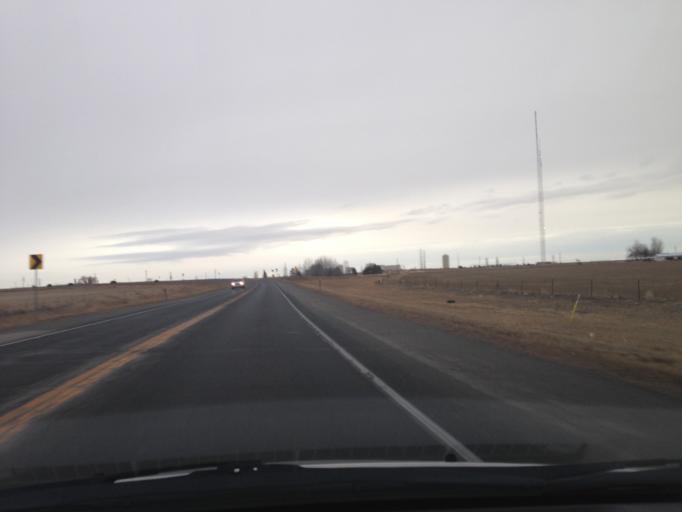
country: US
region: Colorado
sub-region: Weld County
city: Dacono
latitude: 40.0829
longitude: -104.9050
